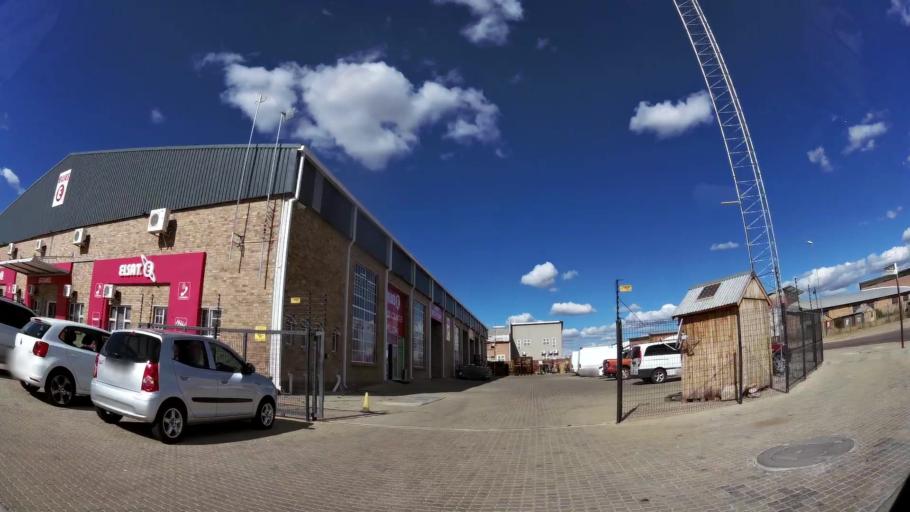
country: ZA
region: Limpopo
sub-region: Capricorn District Municipality
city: Polokwane
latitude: -23.8644
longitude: 29.4771
